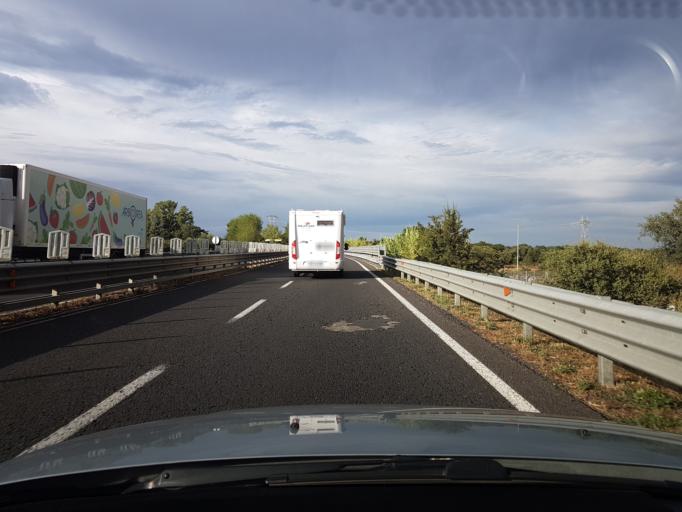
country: IT
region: Sardinia
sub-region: Provincia di Oristano
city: Abbasanta
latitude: 40.1067
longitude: 8.7908
